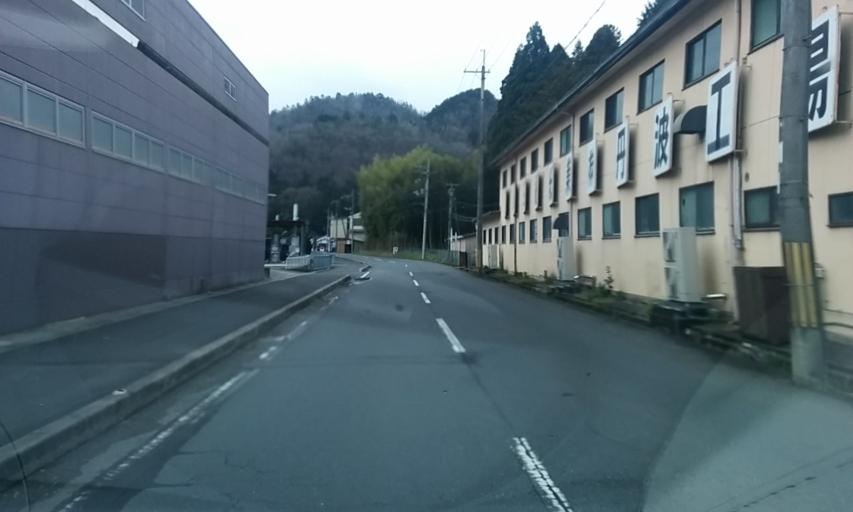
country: JP
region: Kyoto
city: Kameoka
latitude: 35.1403
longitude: 135.4217
